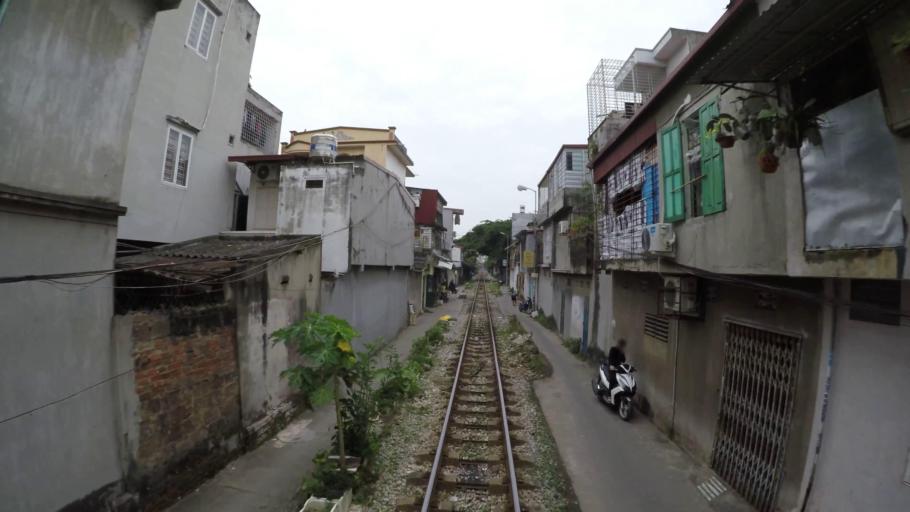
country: VN
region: Hai Phong
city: Haiphong
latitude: 20.8598
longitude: 106.6635
